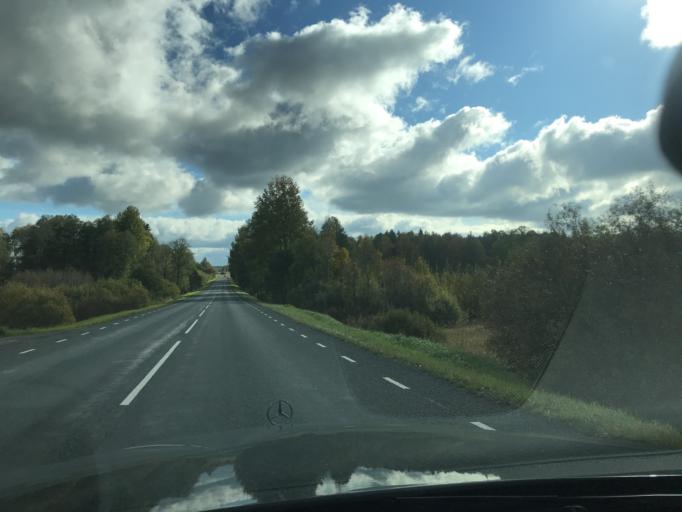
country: EE
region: Vorumaa
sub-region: Antsla vald
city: Vana-Antsla
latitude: 57.9153
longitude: 26.3851
